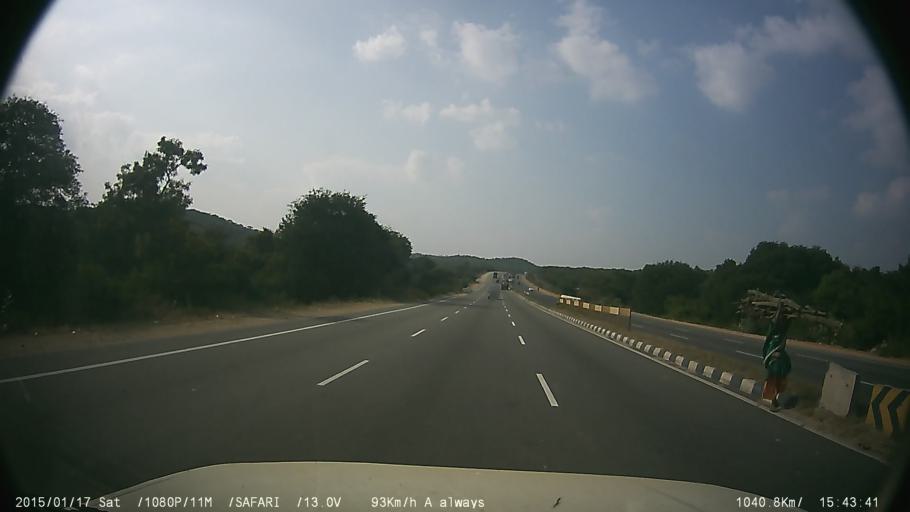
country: IN
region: Tamil Nadu
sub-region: Krishnagiri
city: Hosur
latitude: 12.6899
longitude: 77.9211
